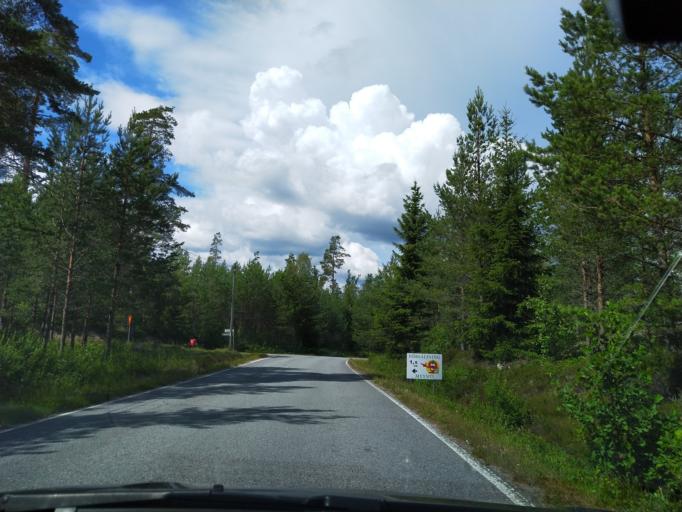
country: FI
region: Uusimaa
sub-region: Raaseporin
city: Karis
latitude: 59.9929
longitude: 23.6895
